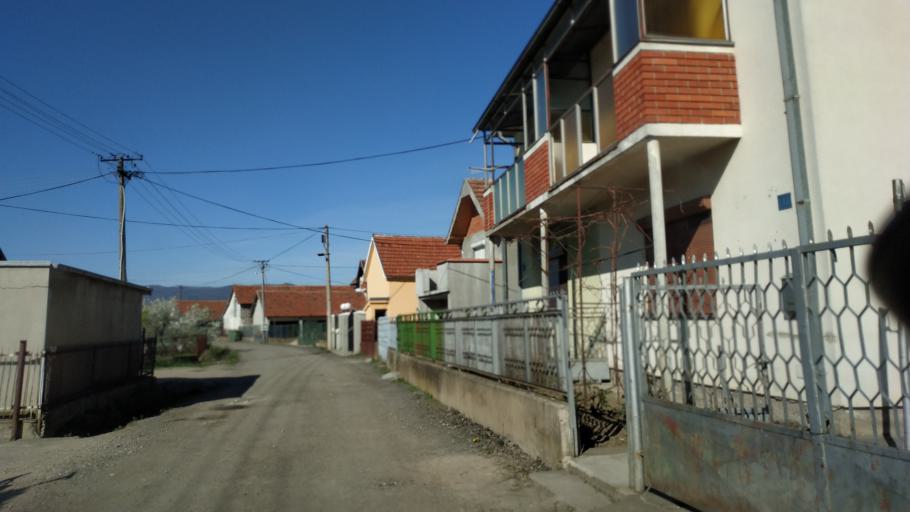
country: RS
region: Central Serbia
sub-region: Nisavski Okrug
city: Aleksinac
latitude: 43.5103
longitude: 21.6869
